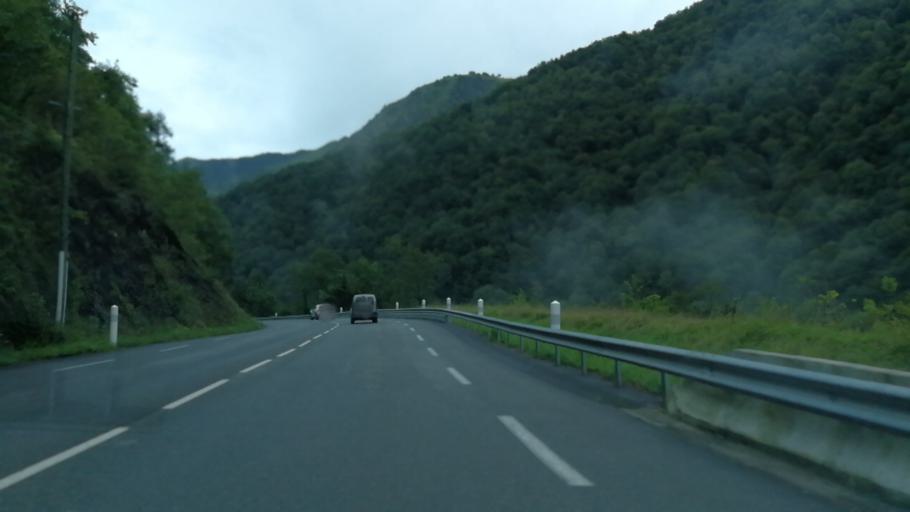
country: FR
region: Aquitaine
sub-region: Departement des Pyrenees-Atlantiques
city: Arette
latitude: 43.0420
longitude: -0.6012
